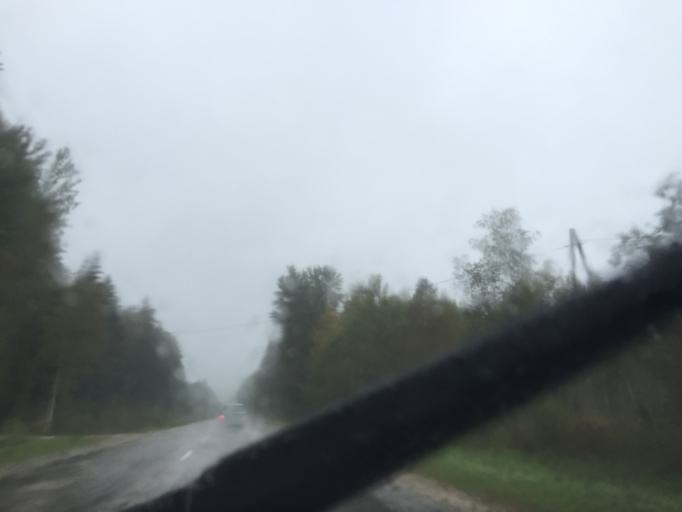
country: LV
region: Ropazu
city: Ropazi
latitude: 56.9893
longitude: 24.6388
